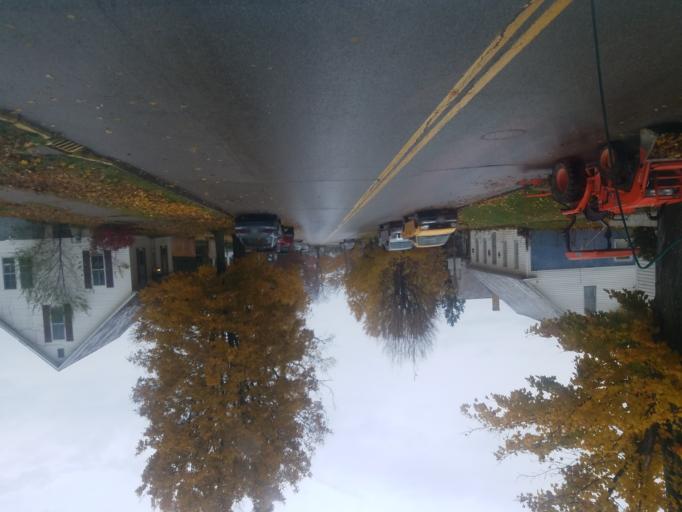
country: US
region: Ohio
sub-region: Morgan County
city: McConnelsville
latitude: 39.4910
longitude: -81.8651
